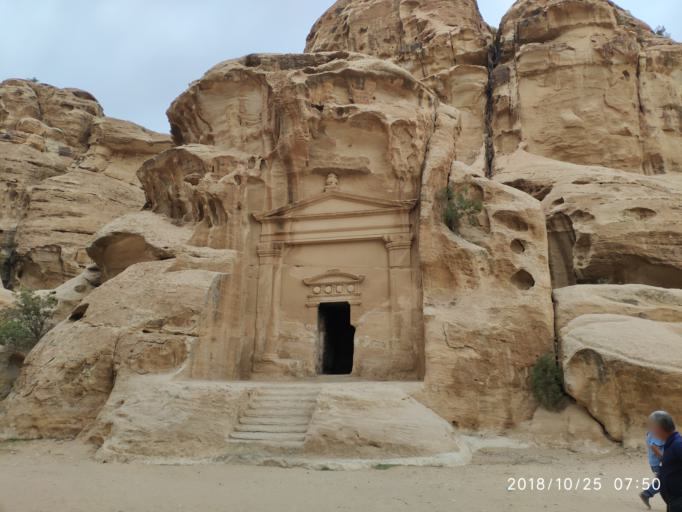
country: JO
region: Ma'an
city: Petra
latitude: 30.3750
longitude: 35.4511
